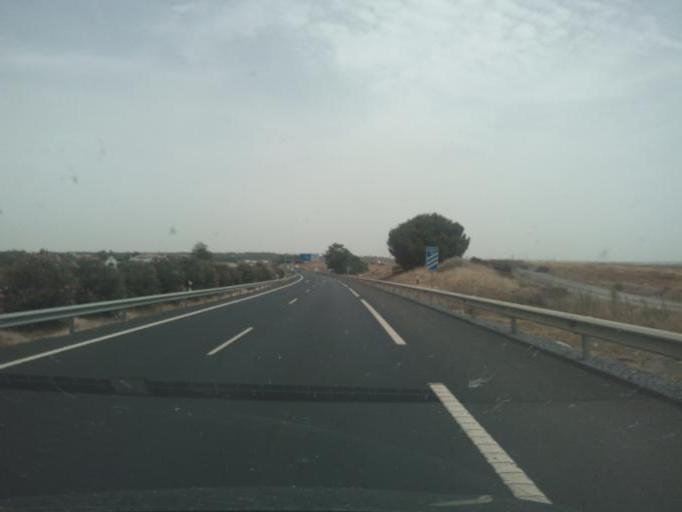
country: ES
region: Andalusia
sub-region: Provincia de Huelva
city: Villarrasa
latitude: 37.3500
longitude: -6.6082
